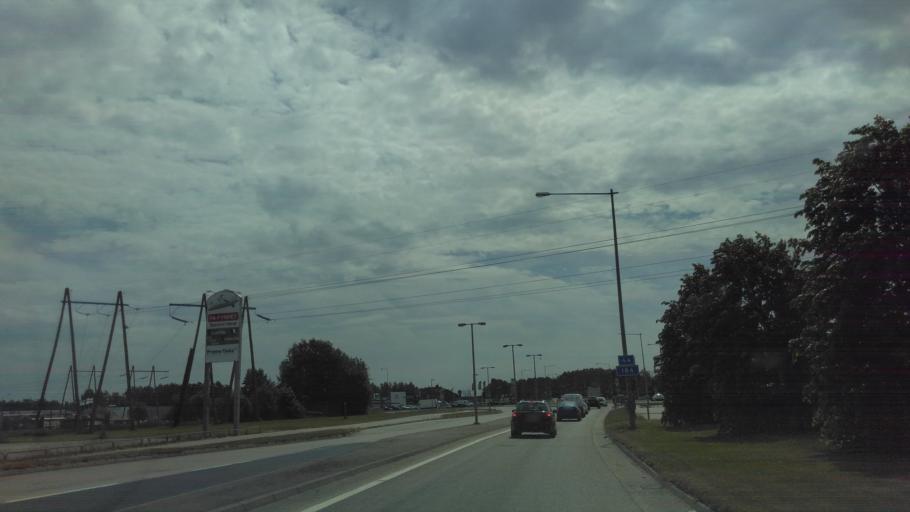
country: SE
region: Vaestra Goetaland
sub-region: Lidkopings Kommun
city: Lidkoping
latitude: 58.4980
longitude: 13.1809
